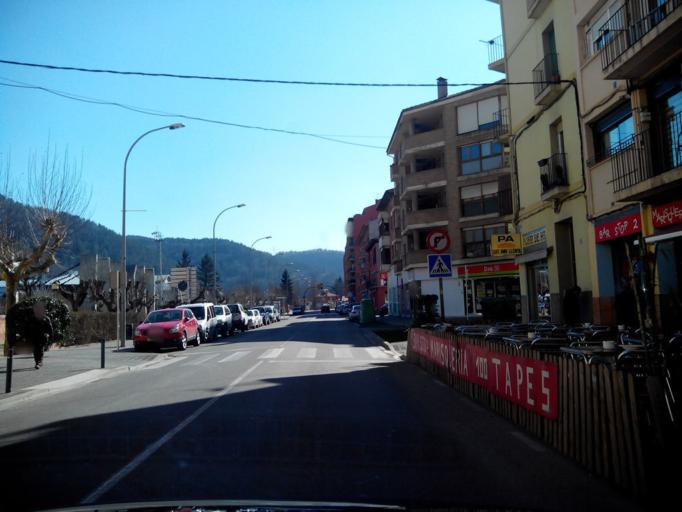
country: ES
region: Catalonia
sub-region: Provincia de Girona
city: Ripoll
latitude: 42.1921
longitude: 2.1935
